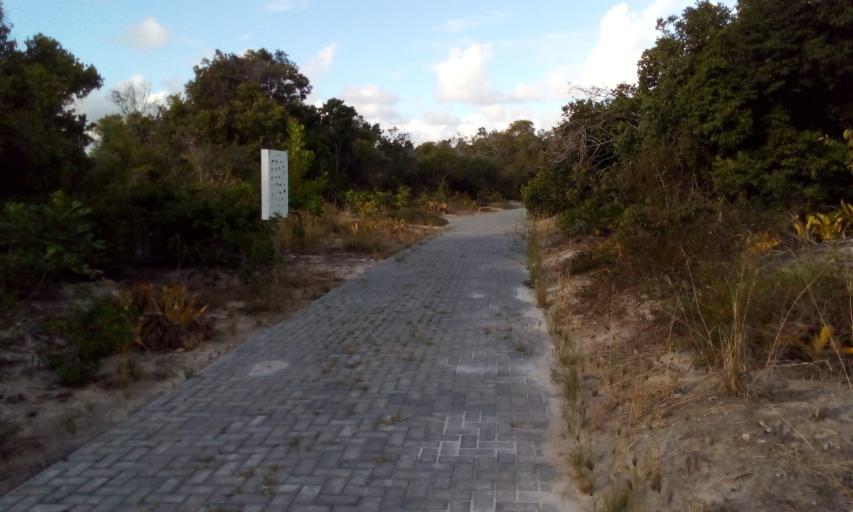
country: BR
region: Bahia
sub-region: Mata De Sao Joao
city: Mata de Sao Joao
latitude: -12.5623
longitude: -38.0002
